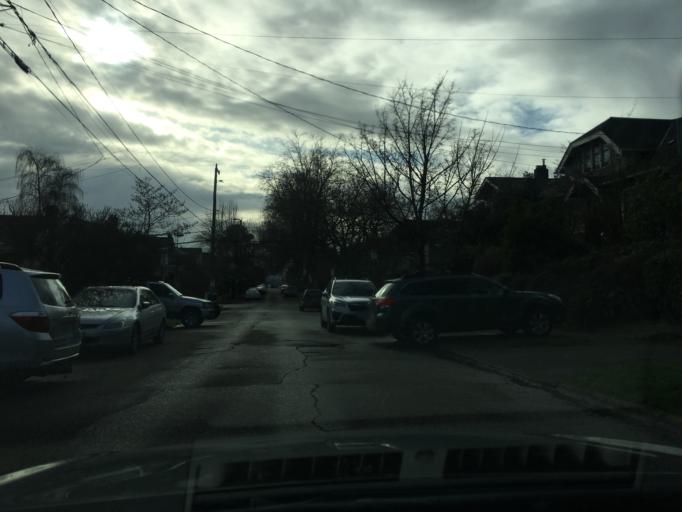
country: US
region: Washington
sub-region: King County
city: Seattle
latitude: 47.6637
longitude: -122.3240
